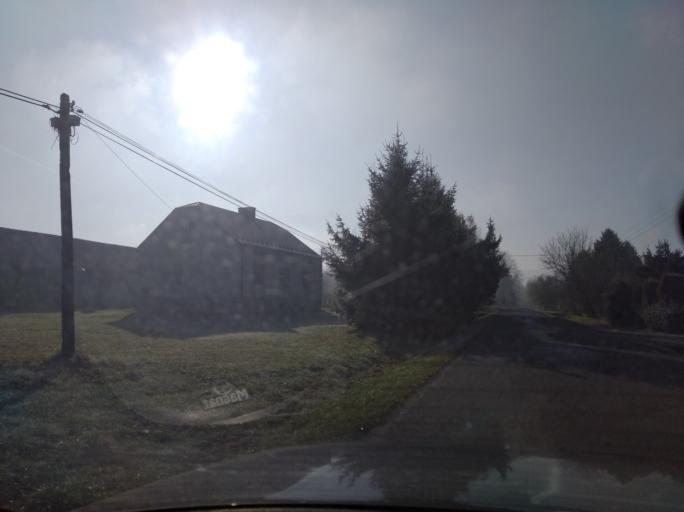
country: PL
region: Subcarpathian Voivodeship
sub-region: Powiat strzyzowski
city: Wysoka Strzyzowska
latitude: 49.8573
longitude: 21.7056
